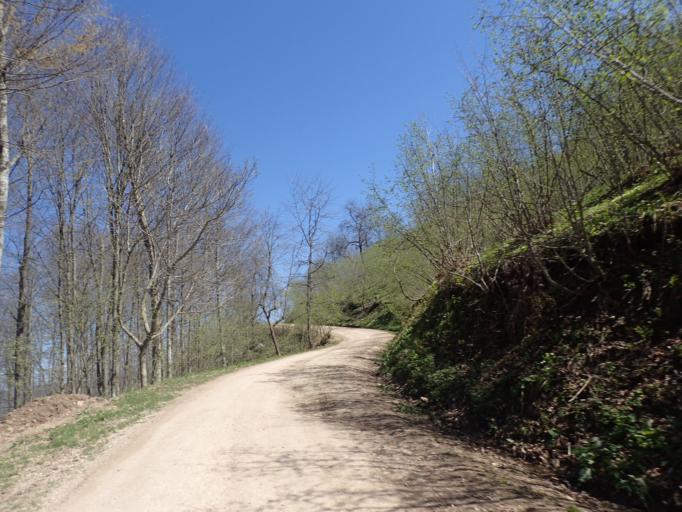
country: TR
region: Ordu
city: Korgan
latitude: 40.7597
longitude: 37.3052
